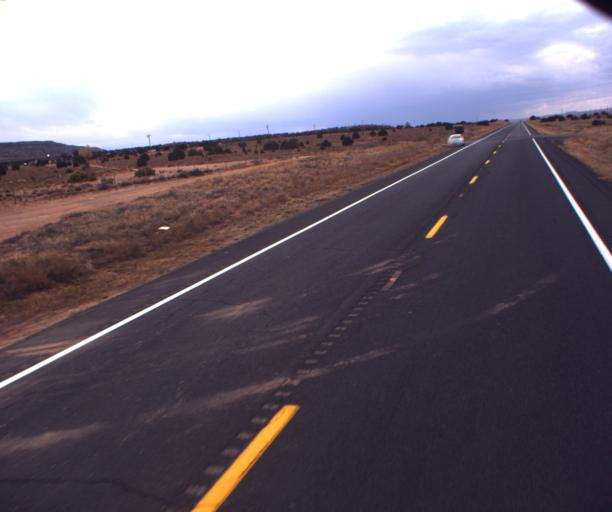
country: US
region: Arizona
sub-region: Coconino County
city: Kaibito
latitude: 36.4132
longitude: -110.8212
